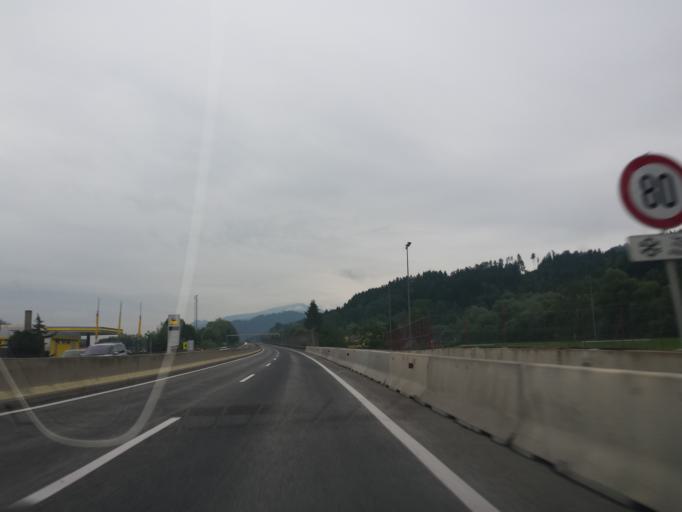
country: AT
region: Styria
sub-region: Politischer Bezirk Bruck-Muerzzuschlag
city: Sankt Marein im Muerztal
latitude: 47.4664
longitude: 15.3722
